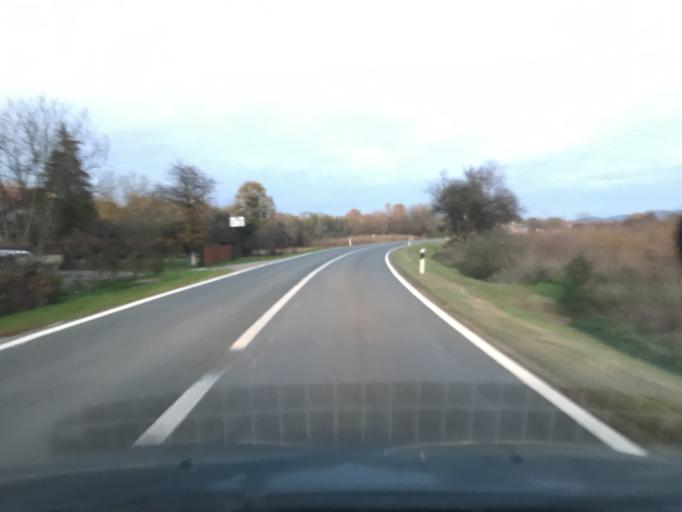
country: HR
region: Sisacko-Moslavacka
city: Novska
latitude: 45.2741
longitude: 16.9100
